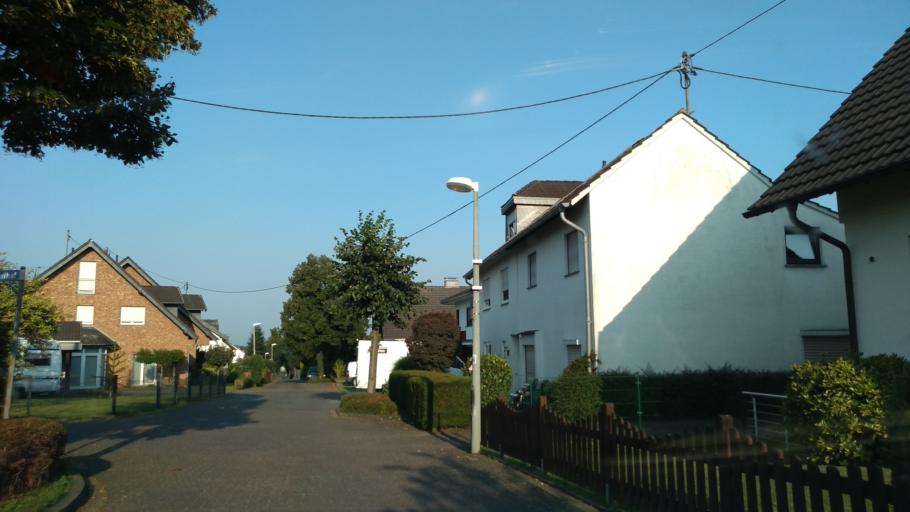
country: DE
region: North Rhine-Westphalia
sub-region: Regierungsbezirk Koln
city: Stossdorf
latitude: 50.8252
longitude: 7.2733
